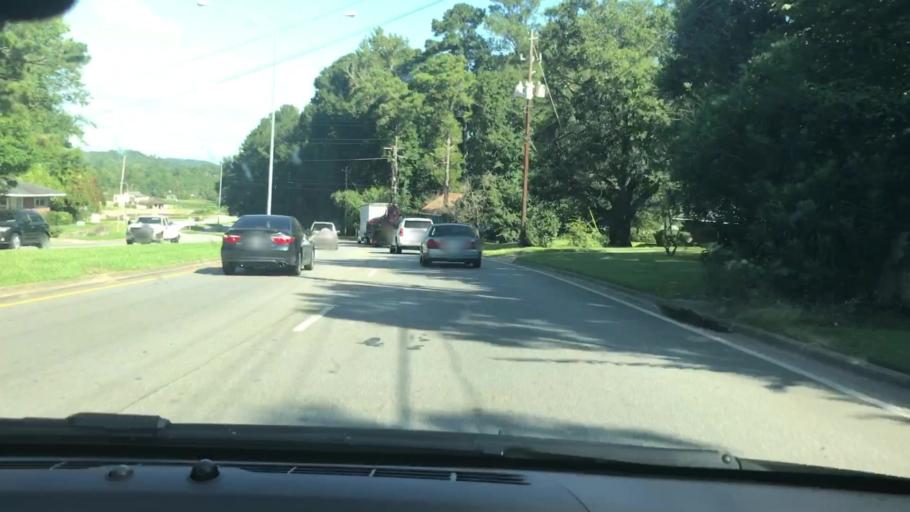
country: US
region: Alabama
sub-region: Barbour County
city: Eufaula
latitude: 31.9030
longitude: -85.1463
